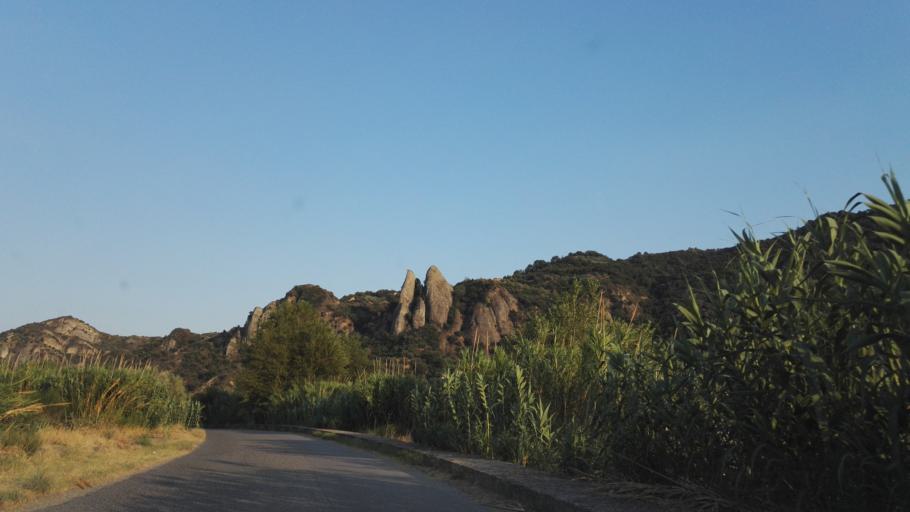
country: IT
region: Calabria
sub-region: Provincia di Reggio Calabria
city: Caulonia
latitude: 38.4046
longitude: 16.3887
